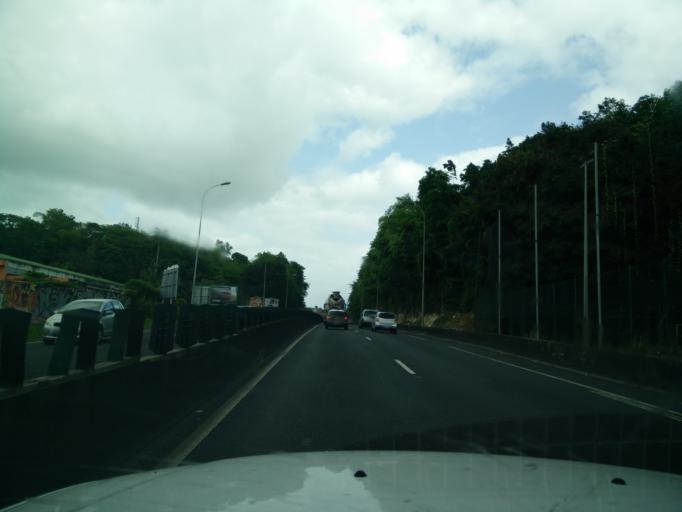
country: GP
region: Guadeloupe
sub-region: Guadeloupe
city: Pointe-a-Pitre
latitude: 16.2464
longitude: -61.5258
